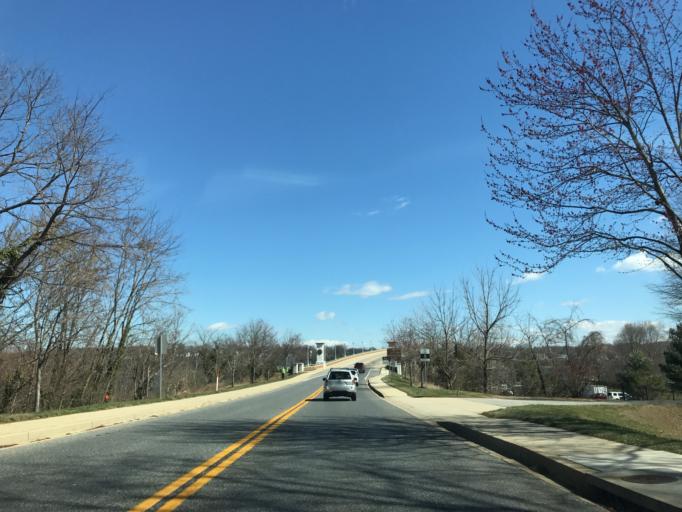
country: US
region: Maryland
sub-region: Anne Arundel County
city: Naval Academy
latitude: 38.9905
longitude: -76.4930
